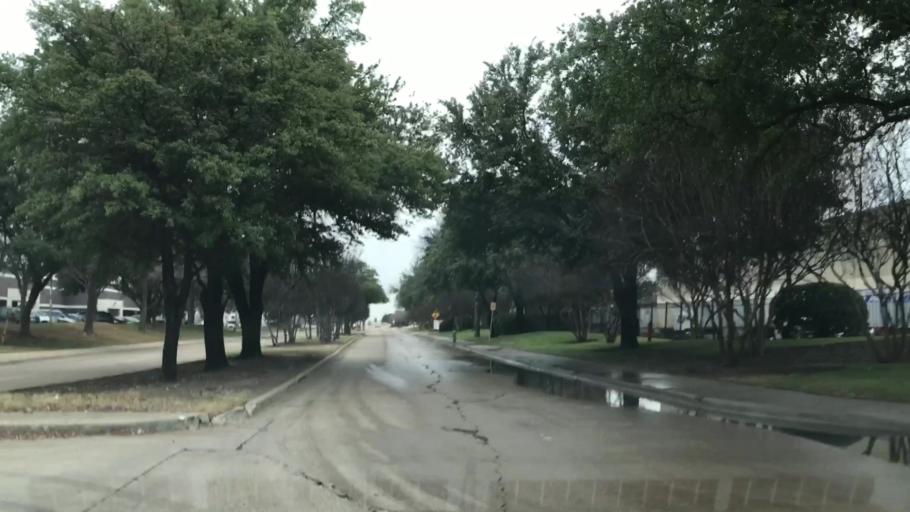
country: US
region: Texas
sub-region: Dallas County
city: Coppell
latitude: 32.9230
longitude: -97.0080
